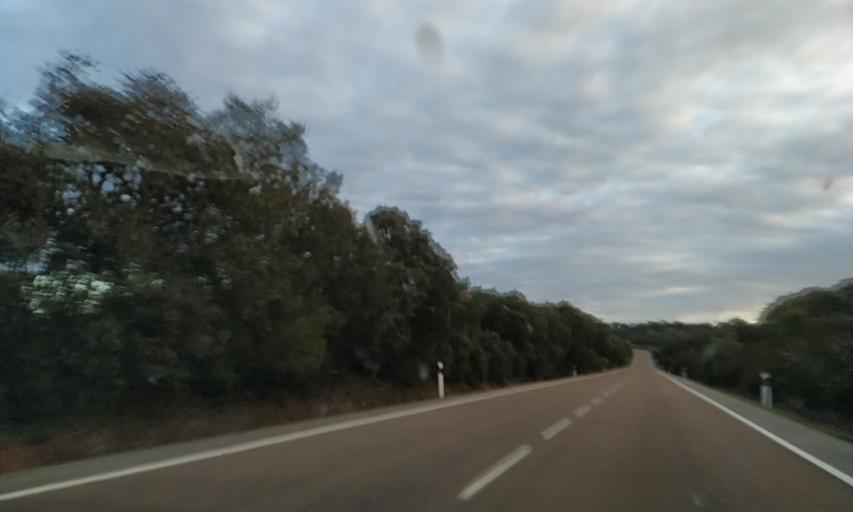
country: ES
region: Extremadura
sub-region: Provincia de Badajoz
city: Puebla de Obando
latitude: 39.2519
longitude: -6.5562
